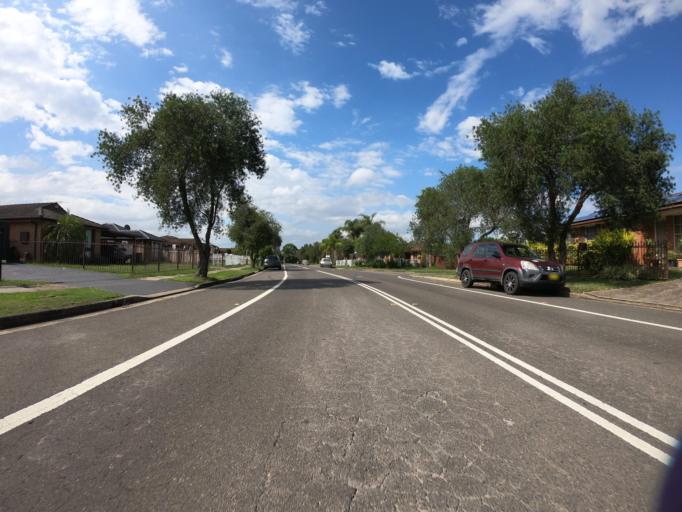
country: AU
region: New South Wales
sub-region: Blacktown
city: Hassall Grove
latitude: -33.7420
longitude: 150.8307
